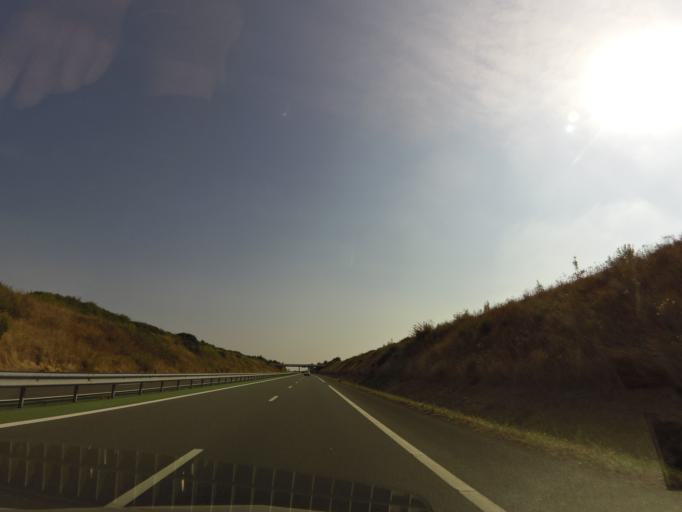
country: FR
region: Pays de la Loire
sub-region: Departement de la Vendee
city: Les Essarts
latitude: 46.7955
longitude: -1.2309
